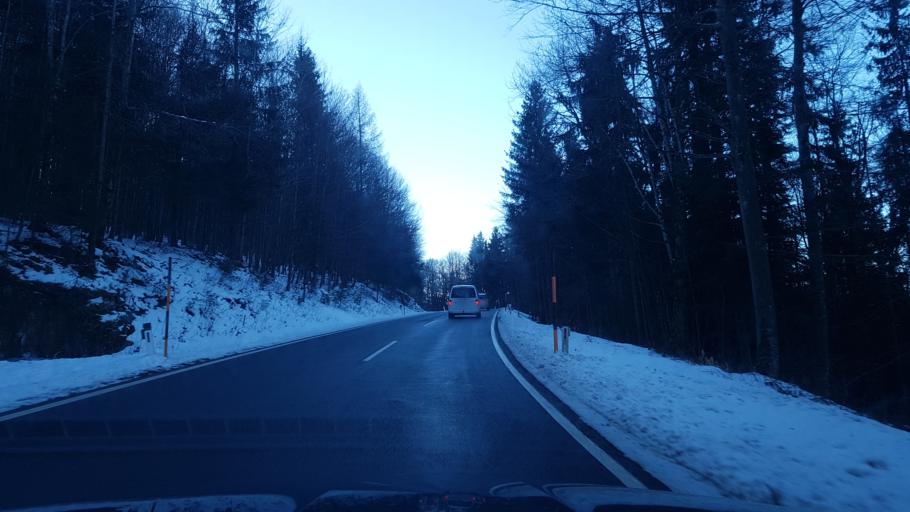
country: AT
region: Salzburg
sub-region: Politischer Bezirk Hallein
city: Krispl
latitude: 47.7145
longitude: 13.1614
